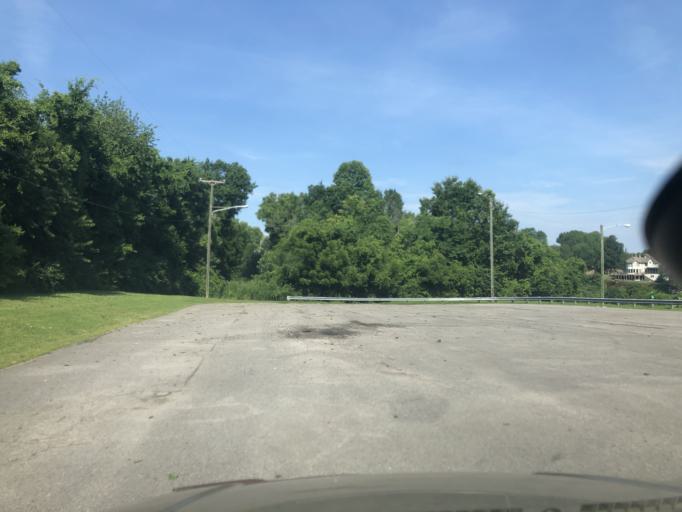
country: US
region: Tennessee
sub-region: Davidson County
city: Lakewood
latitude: 36.2439
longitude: -86.7034
